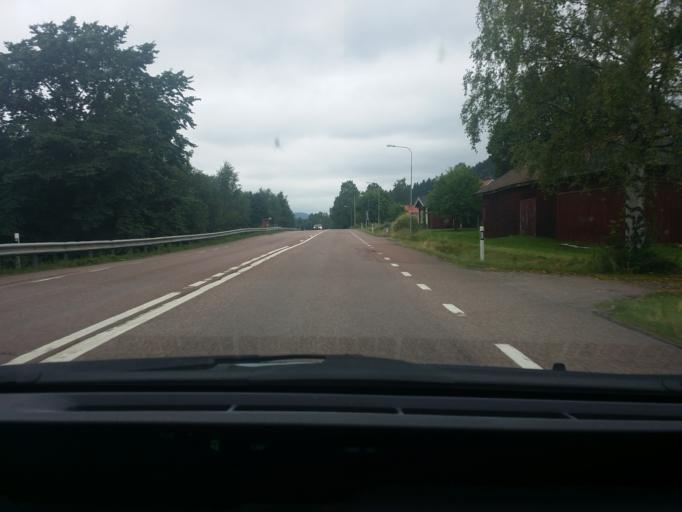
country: SE
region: Dalarna
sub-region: Borlange Kommun
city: Borlaenge
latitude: 60.5334
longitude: 15.3016
